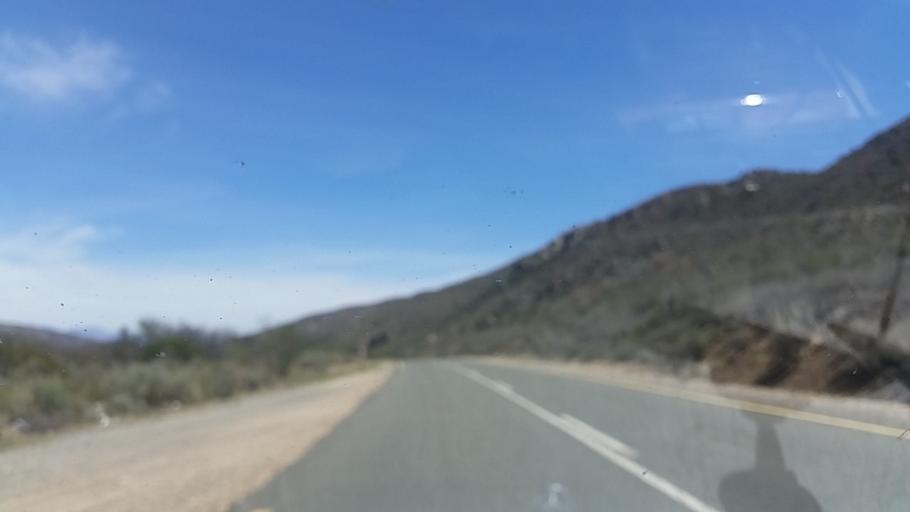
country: ZA
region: Eastern Cape
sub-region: Cacadu District Municipality
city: Willowmore
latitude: -33.3882
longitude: 23.3825
